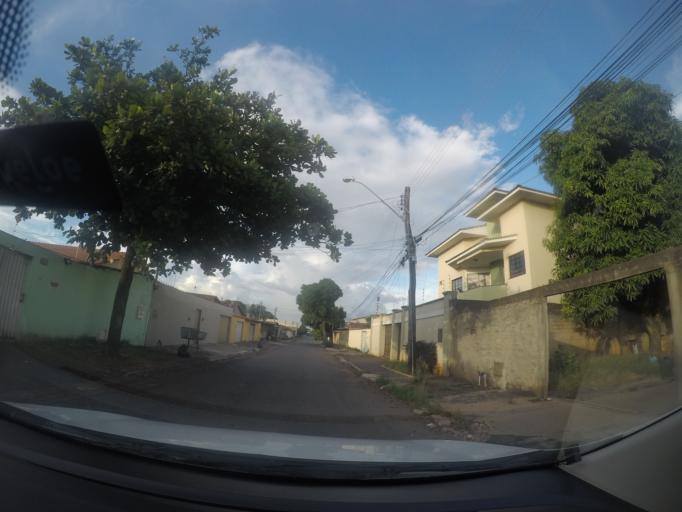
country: BR
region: Goias
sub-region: Goiania
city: Goiania
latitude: -16.6824
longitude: -49.3195
